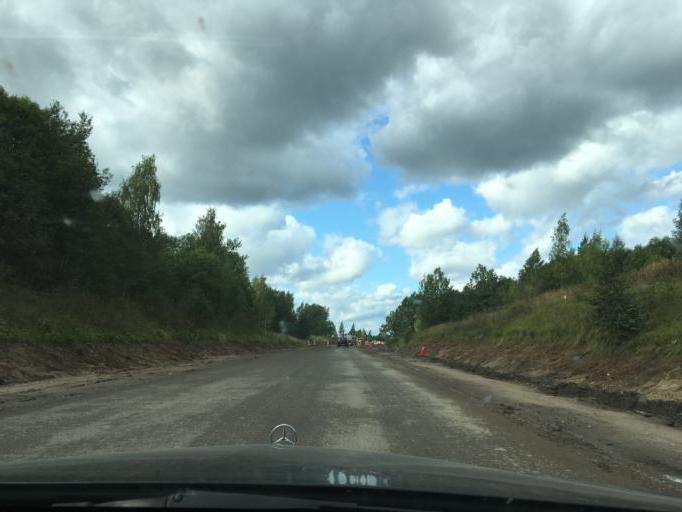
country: RU
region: Pskov
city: Novosokol'niki
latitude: 56.2936
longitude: 30.2358
